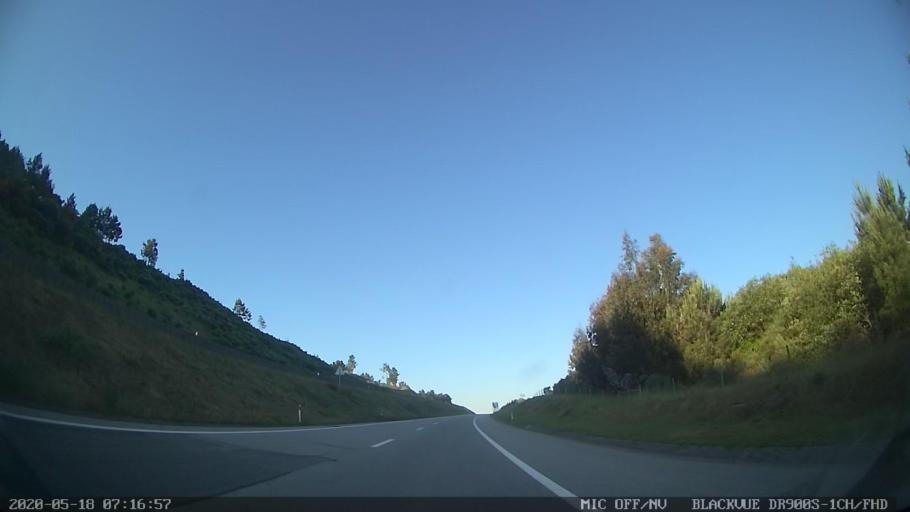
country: PT
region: Vila Real
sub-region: Vila Real
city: Vila Real
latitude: 41.3079
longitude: -7.6880
